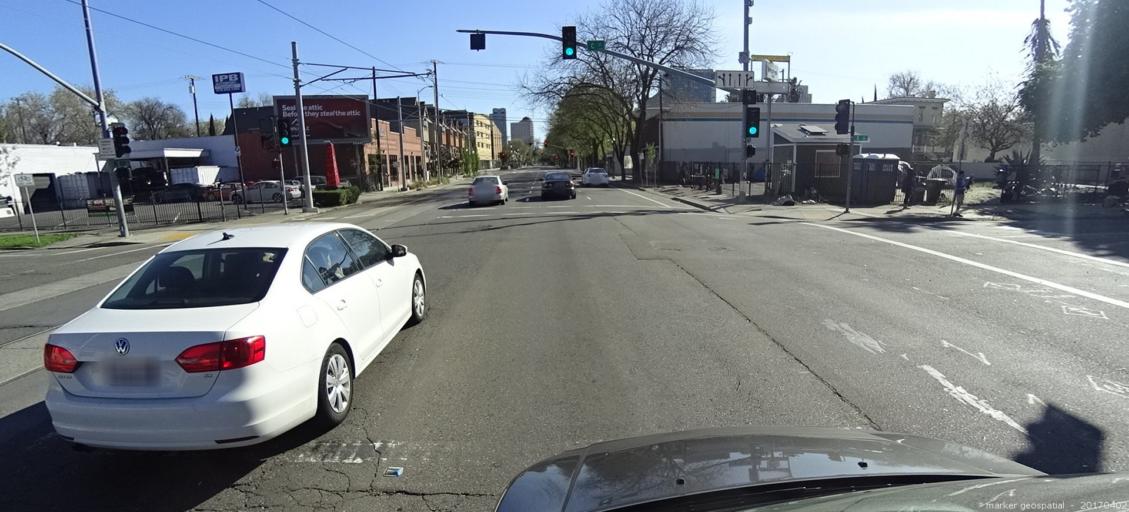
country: US
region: California
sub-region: Sacramento County
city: Sacramento
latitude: 38.5874
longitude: -121.4875
